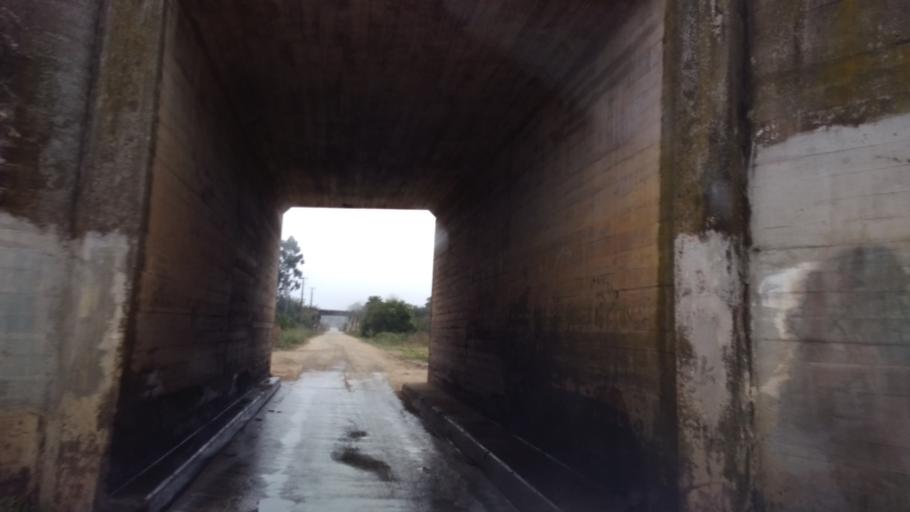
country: UY
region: Florida
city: Florida
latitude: -34.0882
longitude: -56.2079
